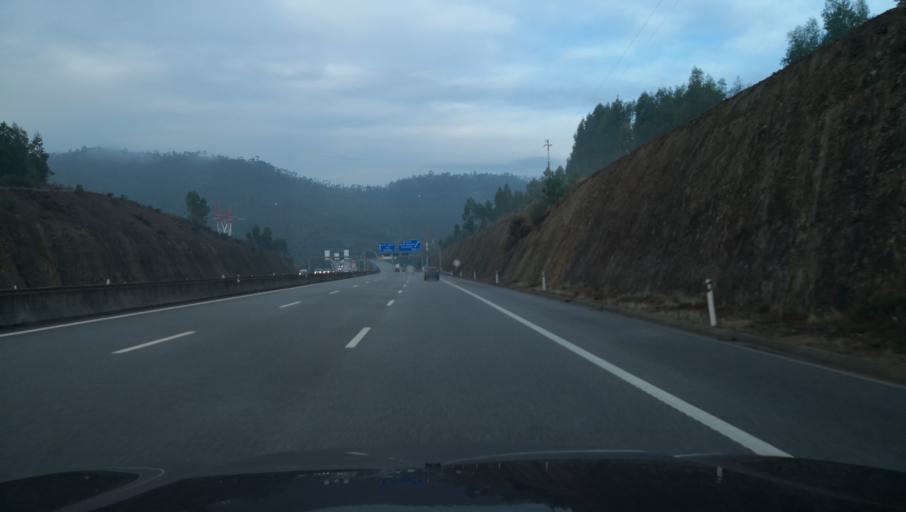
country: PT
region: Porto
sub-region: Paredes
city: Recarei
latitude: 41.1063
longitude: -8.4403
